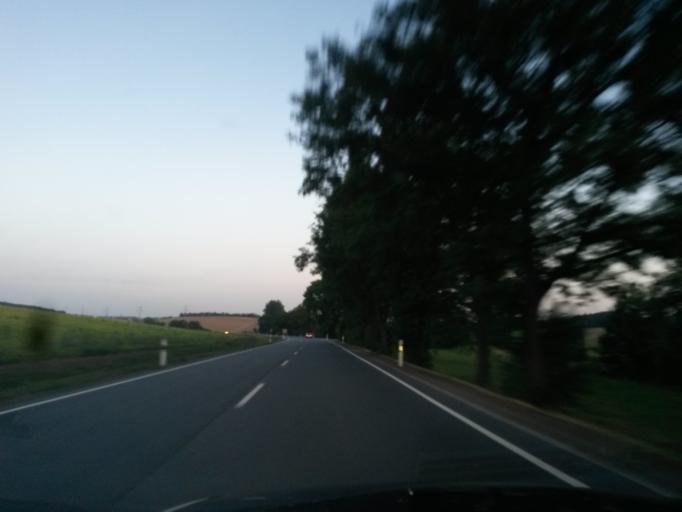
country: DE
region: Bavaria
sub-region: Regierungsbezirk Unterfranken
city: Waldbrunn
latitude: 49.7799
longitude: 9.7731
